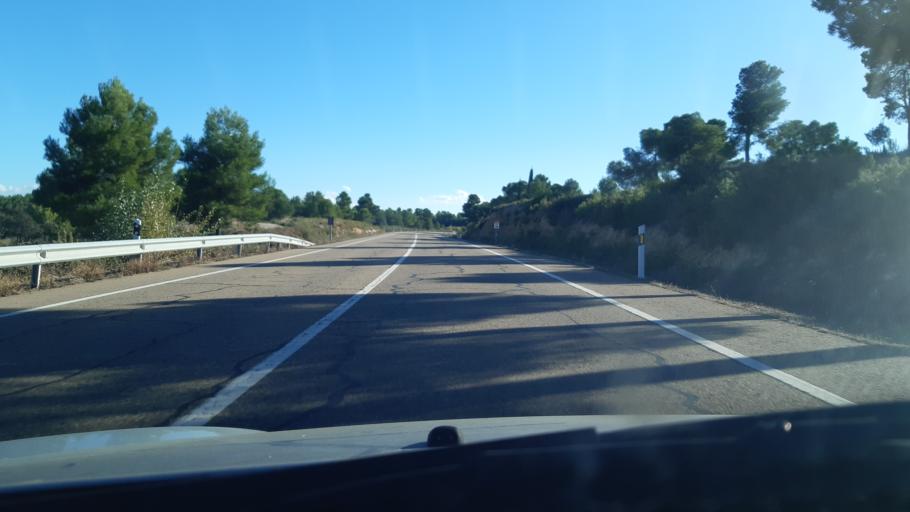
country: ES
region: Aragon
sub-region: Provincia de Teruel
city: Valjunquera
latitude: 40.9412
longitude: -0.0119
